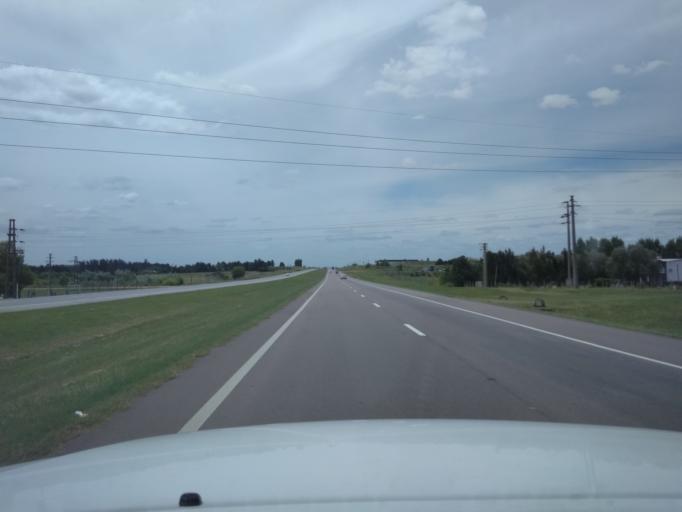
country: UY
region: Canelones
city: Las Piedras
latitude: -34.7125
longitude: -56.2431
